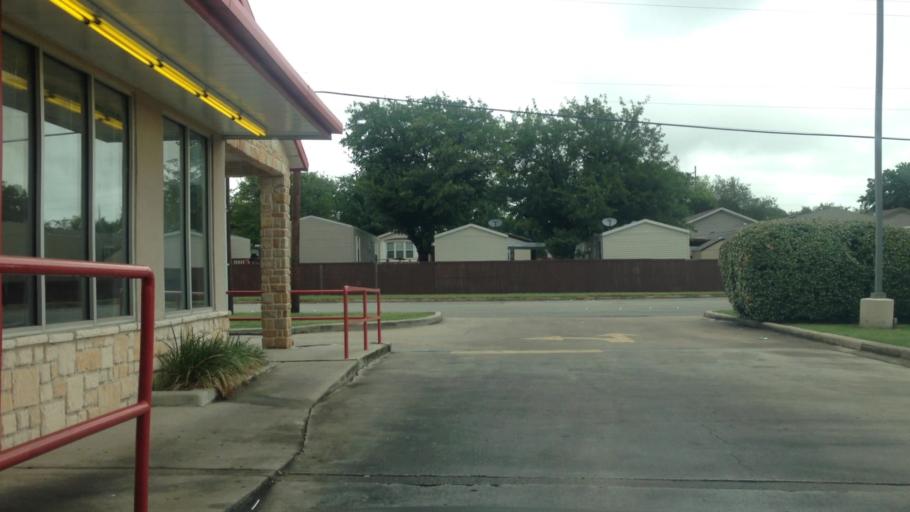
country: US
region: Texas
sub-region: Tarrant County
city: White Settlement
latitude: 32.7658
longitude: -97.4698
